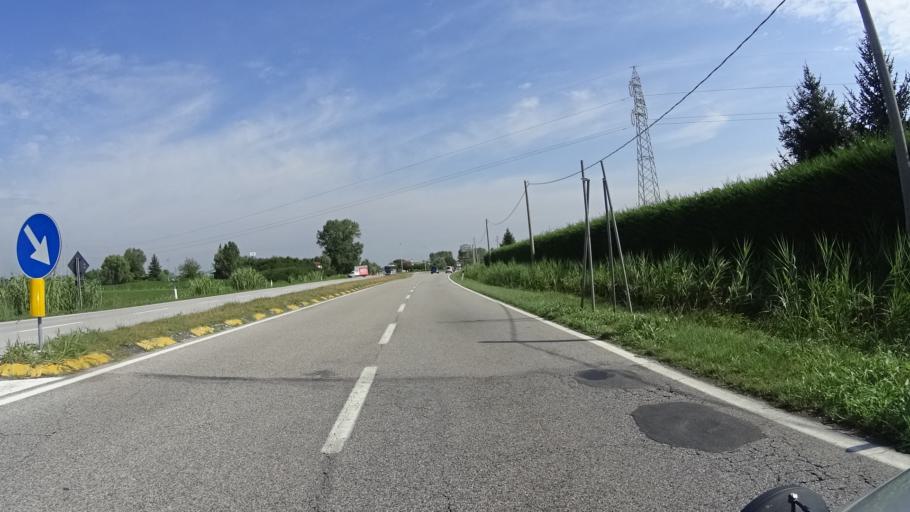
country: IT
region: Friuli Venezia Giulia
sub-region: Provincia di Udine
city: Latisana
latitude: 45.7805
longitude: 13.0215
